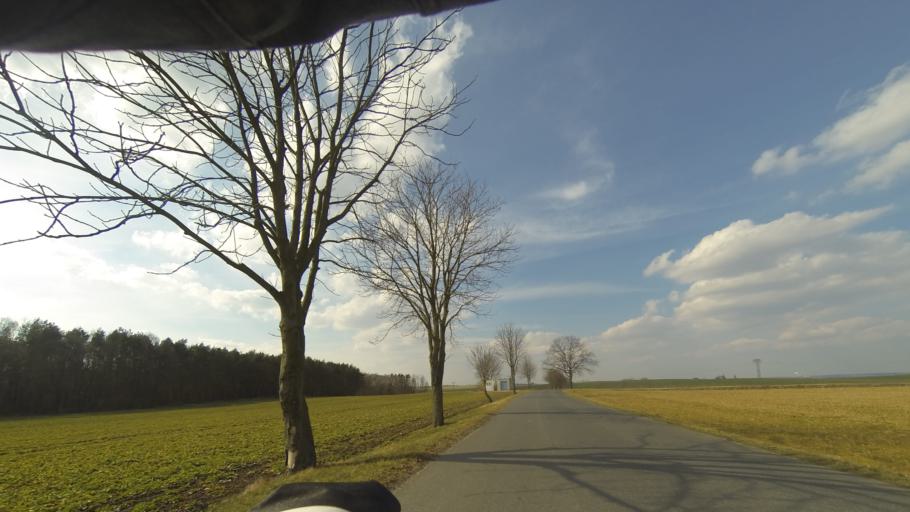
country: DE
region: Saxony
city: Ebersbach
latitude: 51.2153
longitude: 13.6695
